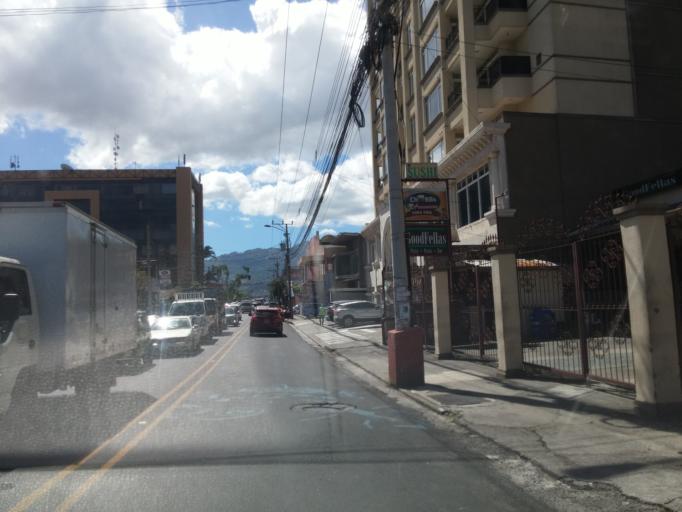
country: CR
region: San Jose
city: San Jose
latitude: 9.9321
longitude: -84.1033
